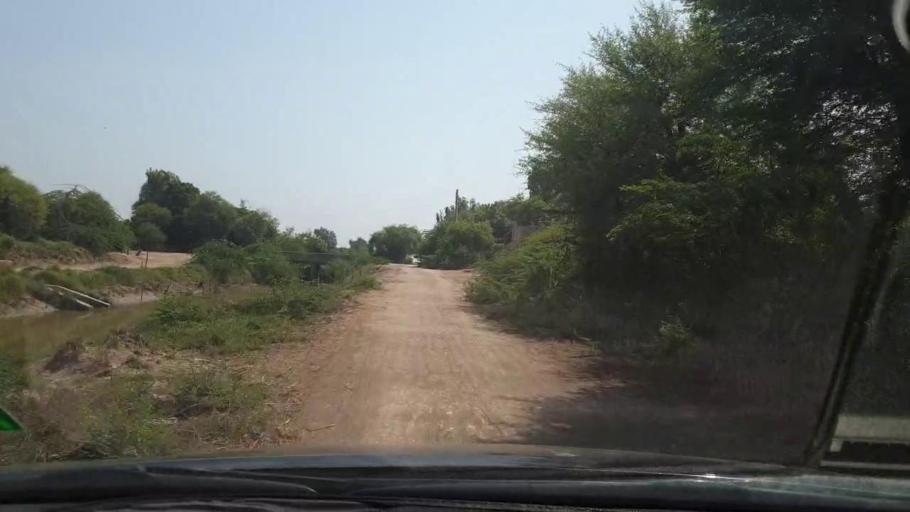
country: PK
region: Sindh
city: Tando Bago
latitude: 24.7842
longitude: 69.1266
